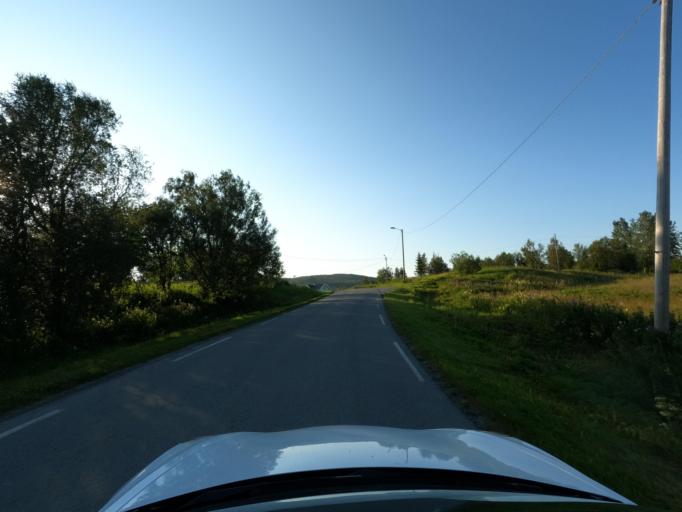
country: NO
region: Troms
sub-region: Skanland
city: Evenskjer
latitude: 68.4647
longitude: 16.6578
